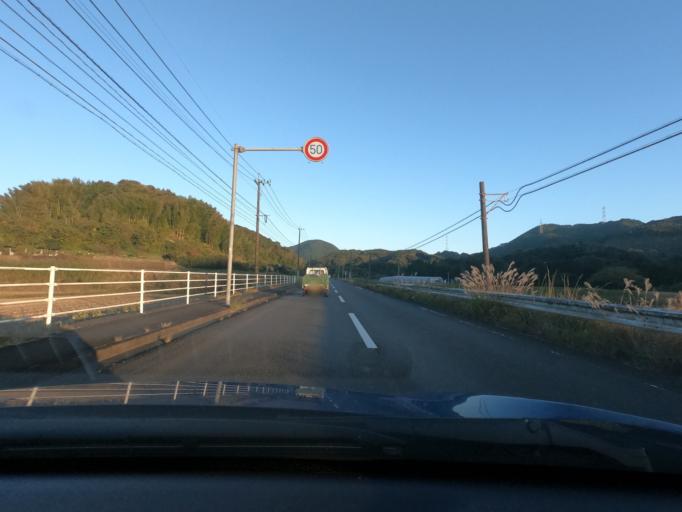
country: JP
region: Kagoshima
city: Satsumasendai
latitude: 31.7907
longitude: 130.4621
